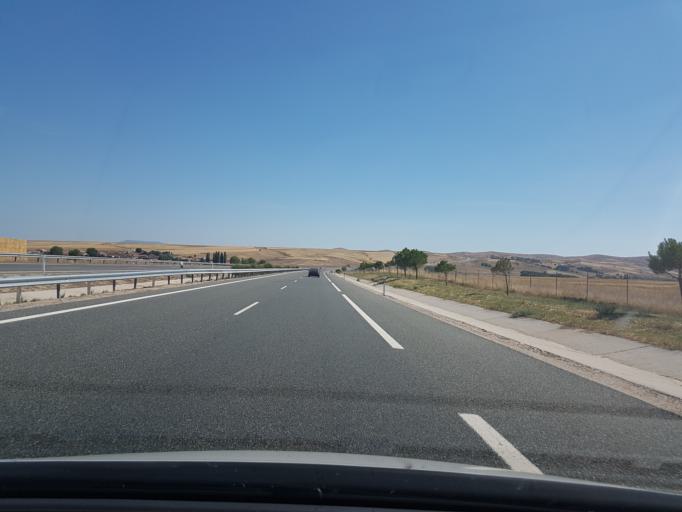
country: ES
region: Castille and Leon
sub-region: Provincia de Avila
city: Monsalupe
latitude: 40.7979
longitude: -4.7783
